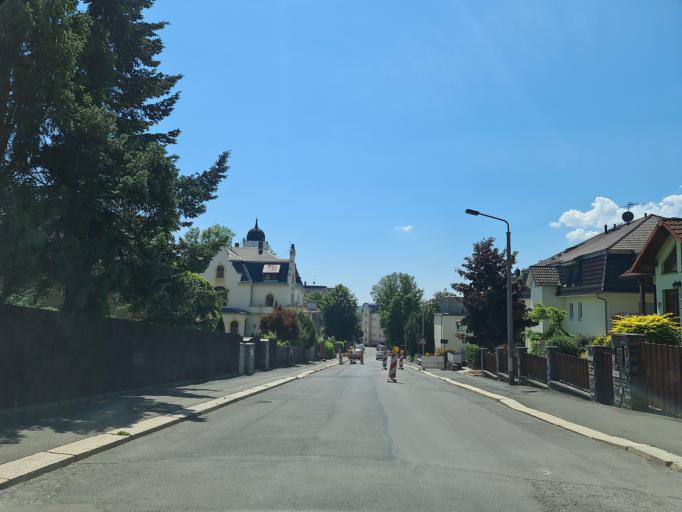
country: DE
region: Saxony
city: Plauen
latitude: 50.4967
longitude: 12.1050
